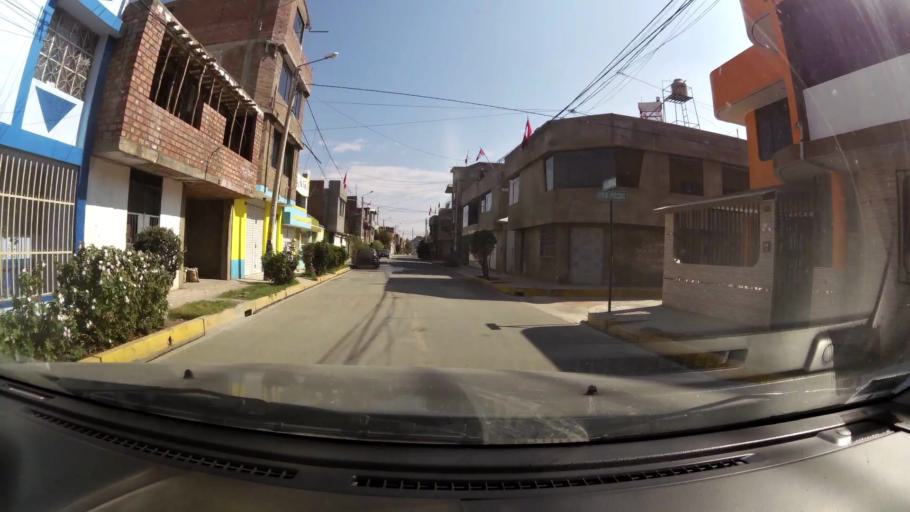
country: PE
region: Junin
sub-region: Provincia de Huancayo
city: El Tambo
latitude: -12.0743
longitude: -75.2255
